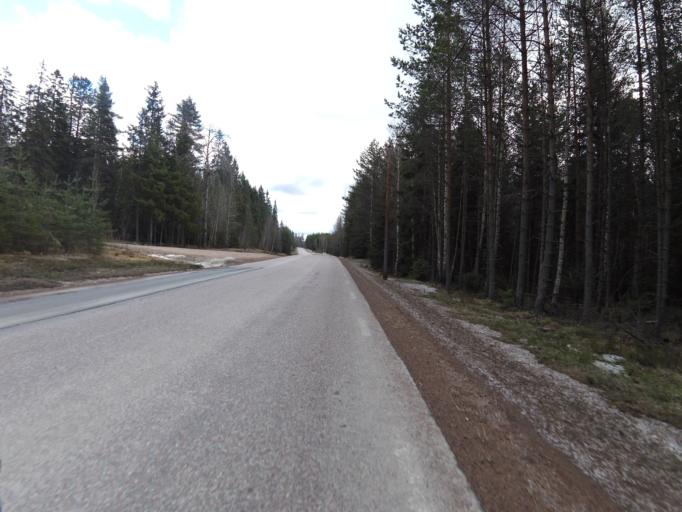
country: SE
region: Dalarna
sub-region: Hedemora Kommun
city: Brunna
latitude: 60.3092
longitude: 16.1679
